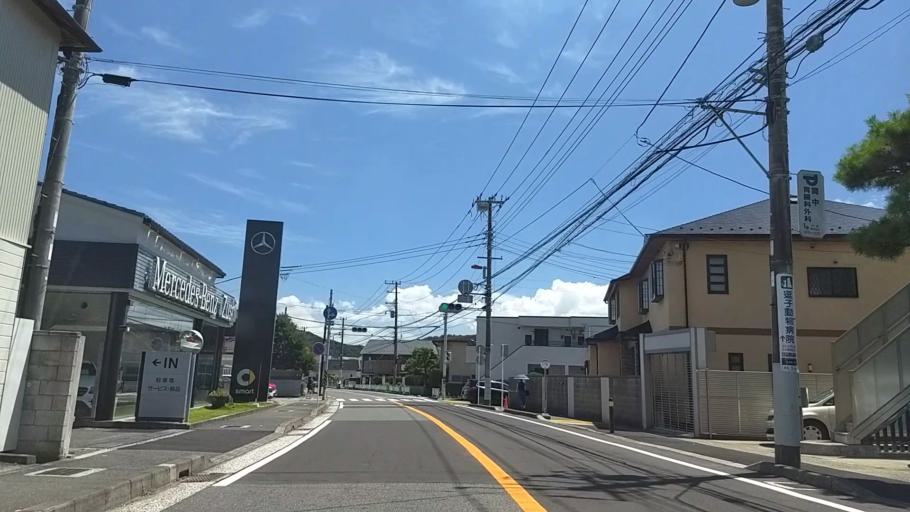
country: JP
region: Kanagawa
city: Zushi
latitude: 35.2999
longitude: 139.5709
